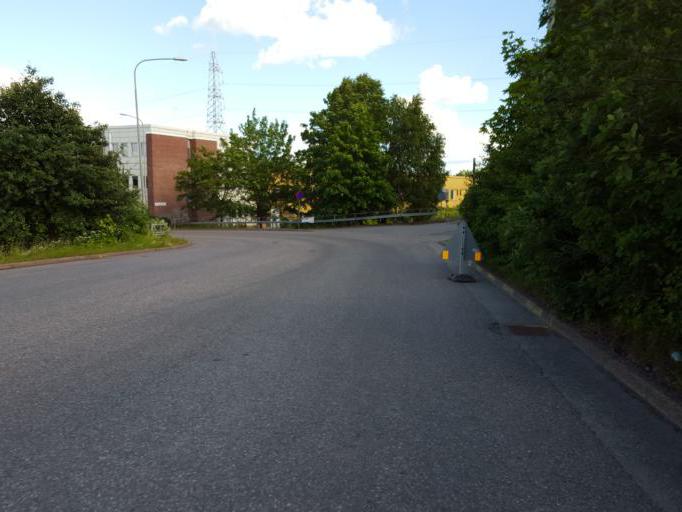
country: SE
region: Stockholm
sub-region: Huddinge Kommun
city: Segeltorp
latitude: 59.2848
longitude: 17.9263
